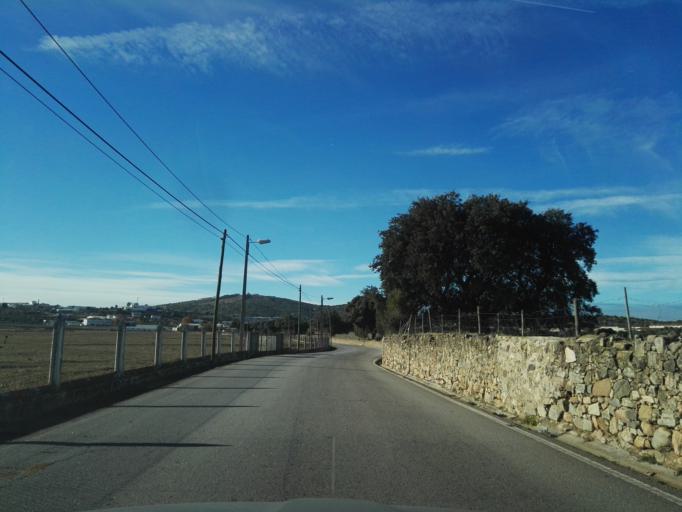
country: PT
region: Portalegre
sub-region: Elvas
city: Elvas
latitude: 38.8887
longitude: -7.1322
